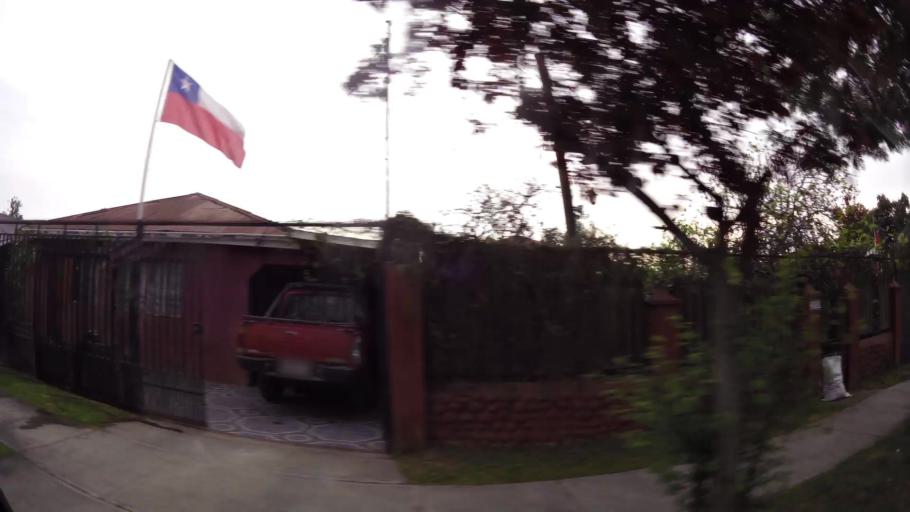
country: CL
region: Santiago Metropolitan
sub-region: Provincia de Santiago
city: Lo Prado
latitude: -33.5109
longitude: -70.7691
